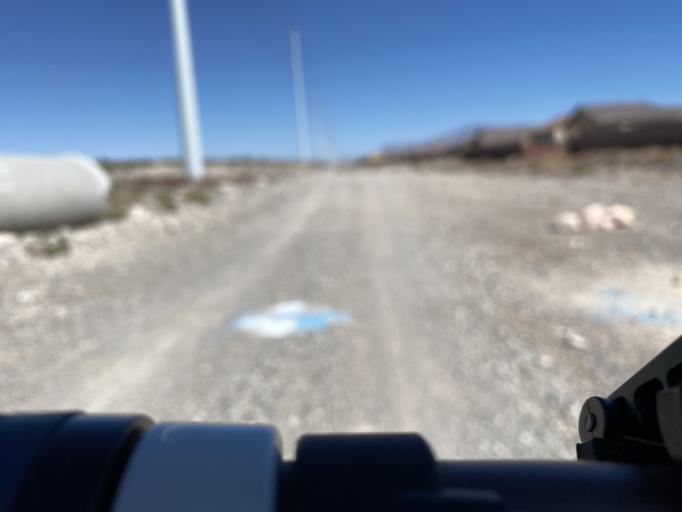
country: US
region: Nevada
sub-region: Clark County
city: Summerlin South
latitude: 36.2917
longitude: -115.3334
